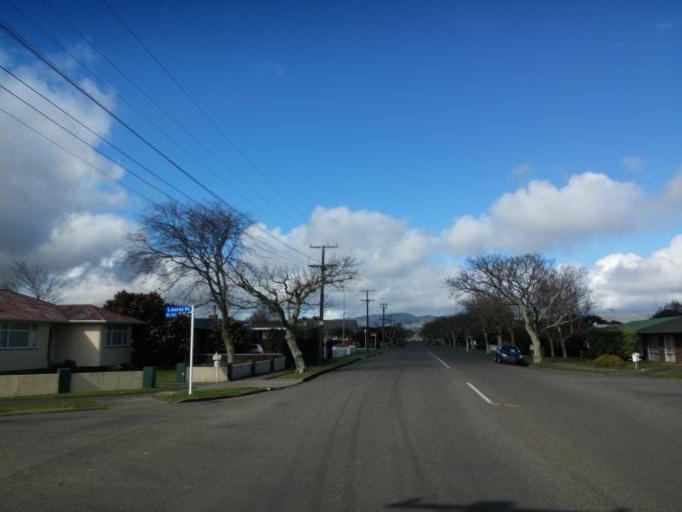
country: NZ
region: Manawatu-Wanganui
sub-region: Palmerston North City
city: Palmerston North
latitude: -40.3717
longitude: 175.5789
